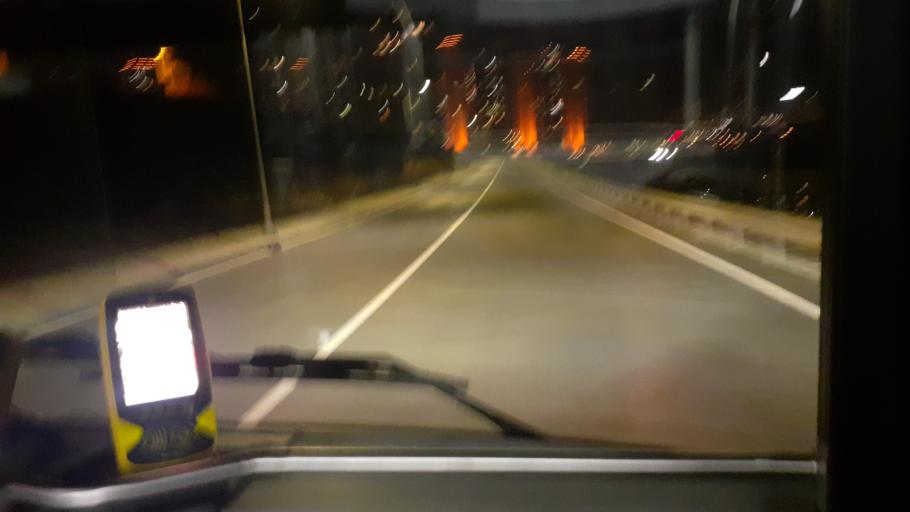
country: TR
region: Istanbul
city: Basaksehir
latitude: 41.0727
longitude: 28.7771
